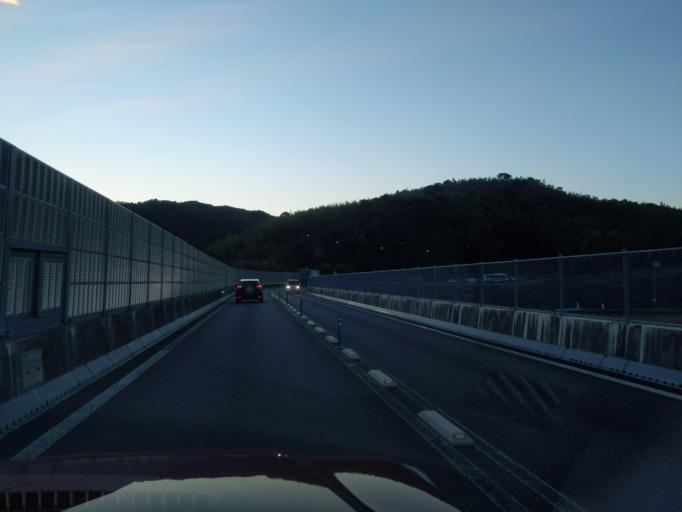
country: JP
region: Tokushima
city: Anan
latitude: 33.8023
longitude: 134.5925
